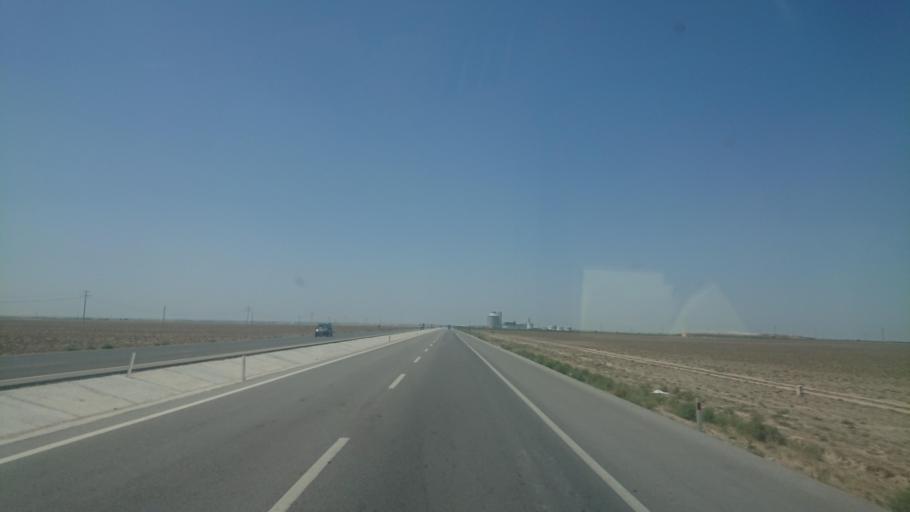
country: TR
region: Aksaray
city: Sultanhani
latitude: 38.2754
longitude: 33.6907
